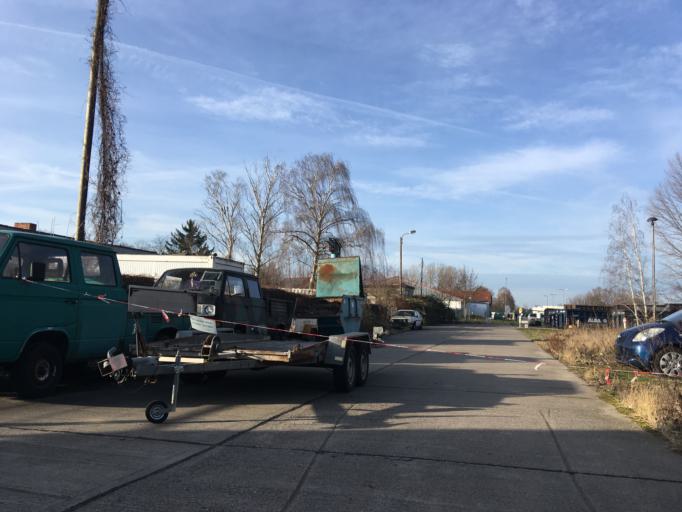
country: DE
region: Berlin
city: Heinersdorf
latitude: 52.5701
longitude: 13.4449
